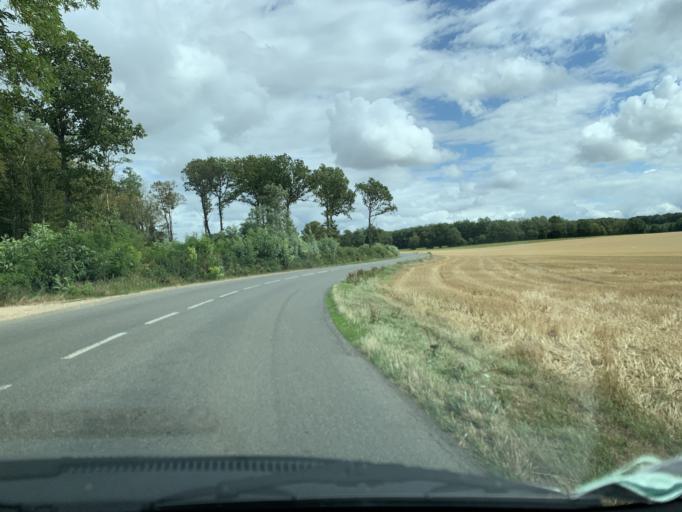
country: FR
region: Bourgogne
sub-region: Departement de la Nievre
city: Clamecy
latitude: 47.4467
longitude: 3.5173
